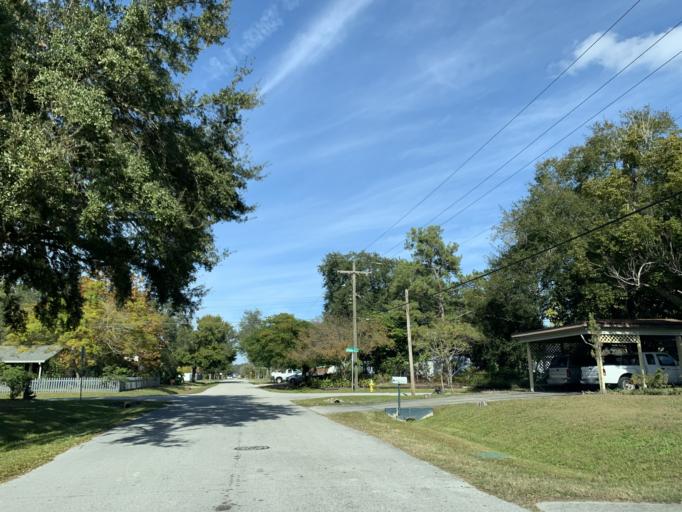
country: US
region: Florida
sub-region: Hillsborough County
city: Tampa
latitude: 27.8880
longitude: -82.5001
